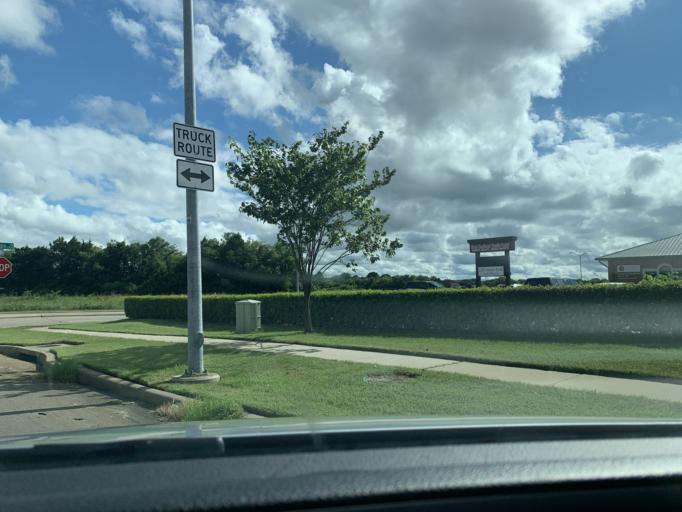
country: US
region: Texas
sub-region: Dallas County
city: Grand Prairie
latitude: 32.6728
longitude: -97.0381
